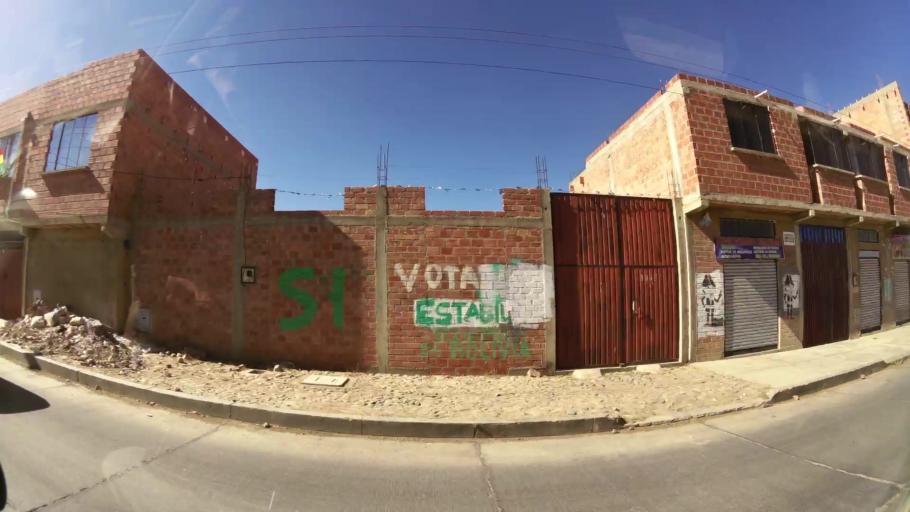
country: BO
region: La Paz
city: La Paz
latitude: -16.5297
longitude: -68.2088
